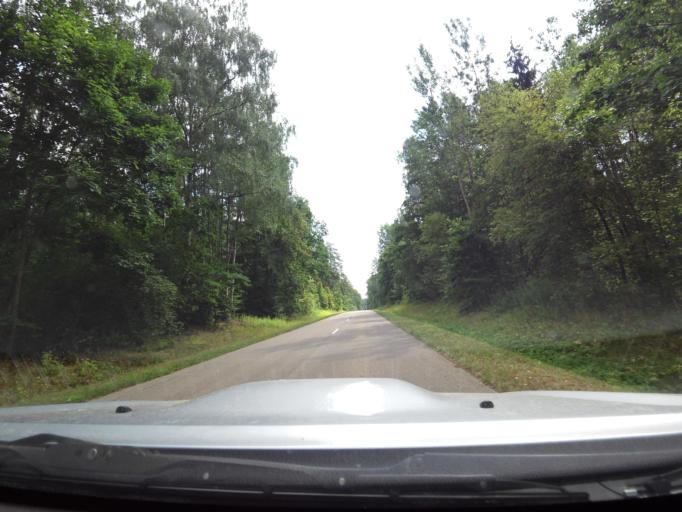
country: RU
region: Kaliningrad
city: Neman
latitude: 55.0895
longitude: 22.0345
